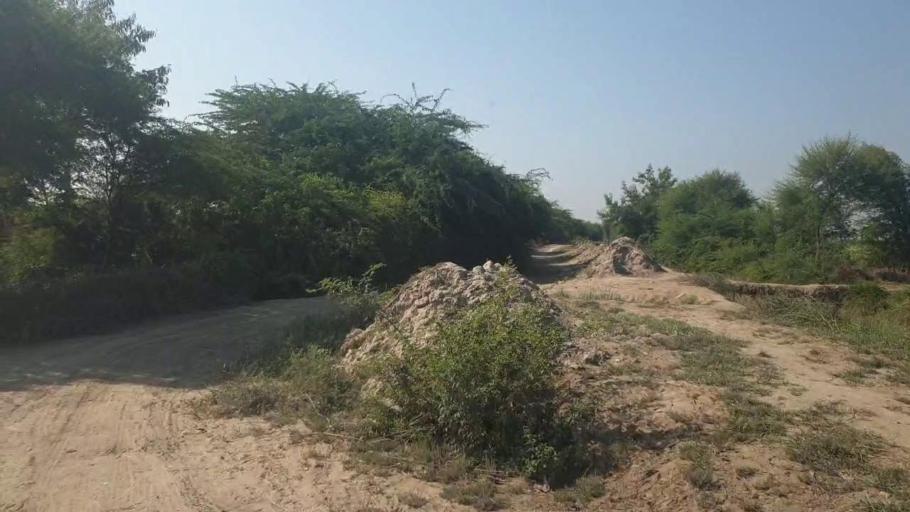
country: PK
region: Sindh
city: Badin
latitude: 24.7267
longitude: 68.8811
